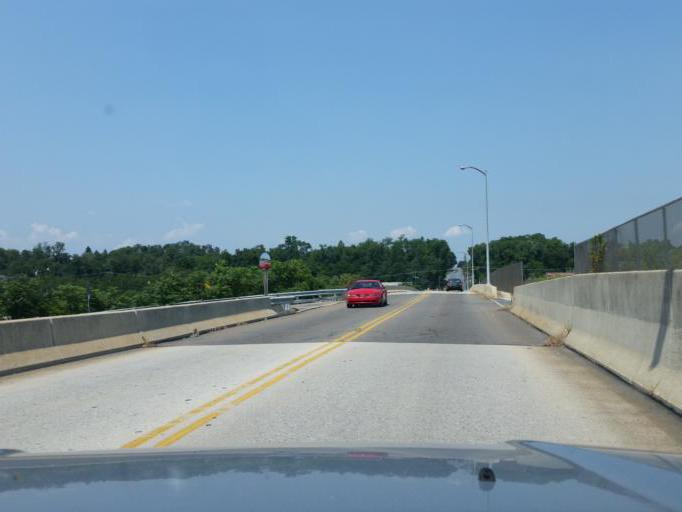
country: US
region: Pennsylvania
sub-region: Dauphin County
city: Rutherford
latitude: 40.2618
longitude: -76.7777
